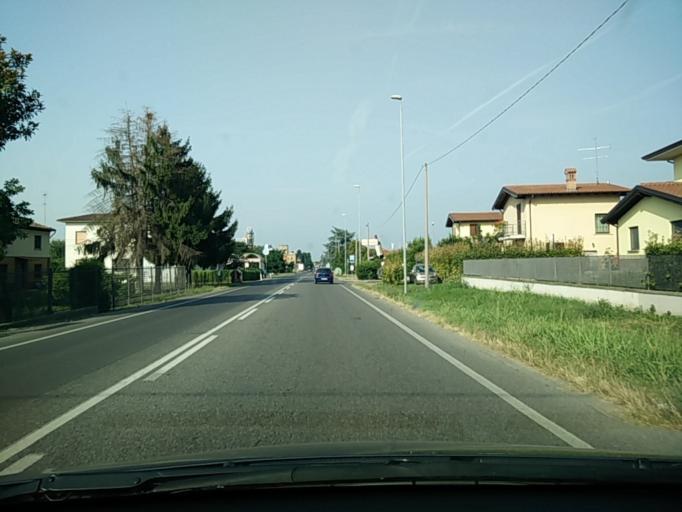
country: IT
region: Lombardy
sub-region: Provincia di Pavia
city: Santa Giuletta
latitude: 45.0312
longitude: 9.1714
